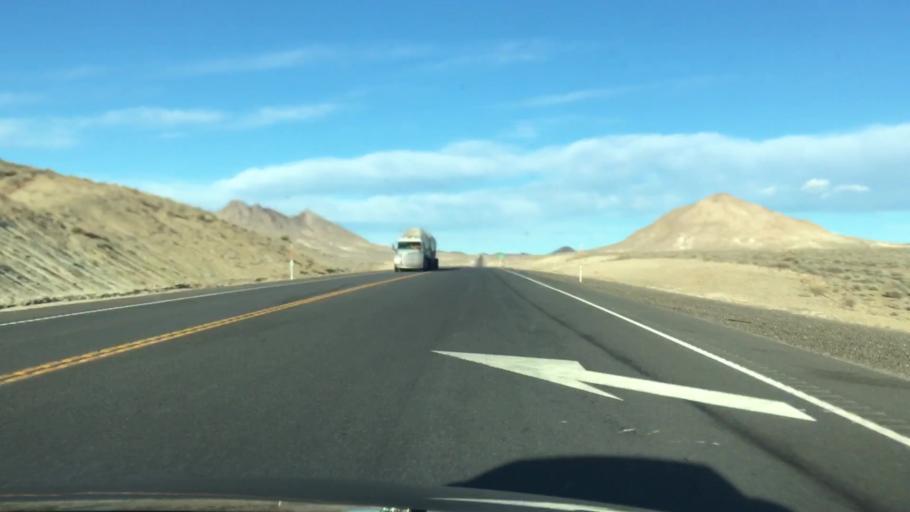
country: US
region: Nevada
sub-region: Nye County
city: Tonopah
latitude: 38.0074
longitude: -117.2600
